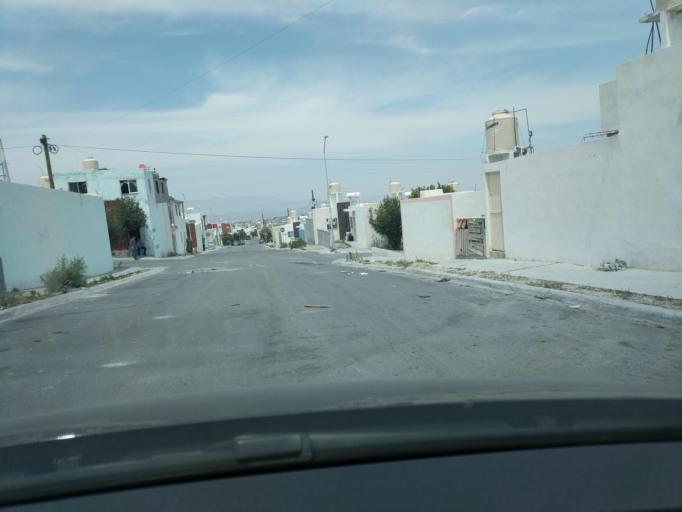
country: MX
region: Coahuila
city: Saltillo
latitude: 25.3454
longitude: -101.0059
